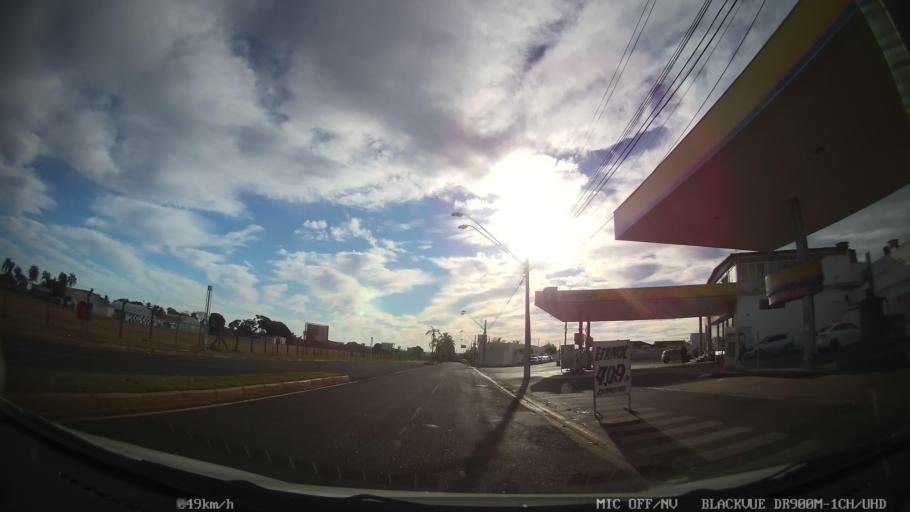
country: BR
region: Sao Paulo
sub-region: Catanduva
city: Catanduva
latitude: -21.1471
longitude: -48.9856
